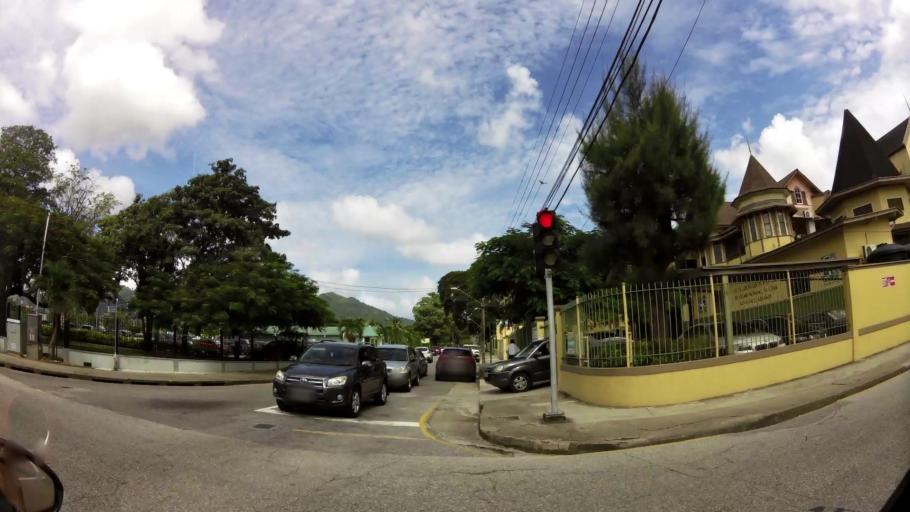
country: TT
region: City of Port of Spain
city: Port-of-Spain
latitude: 10.6681
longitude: -61.5228
